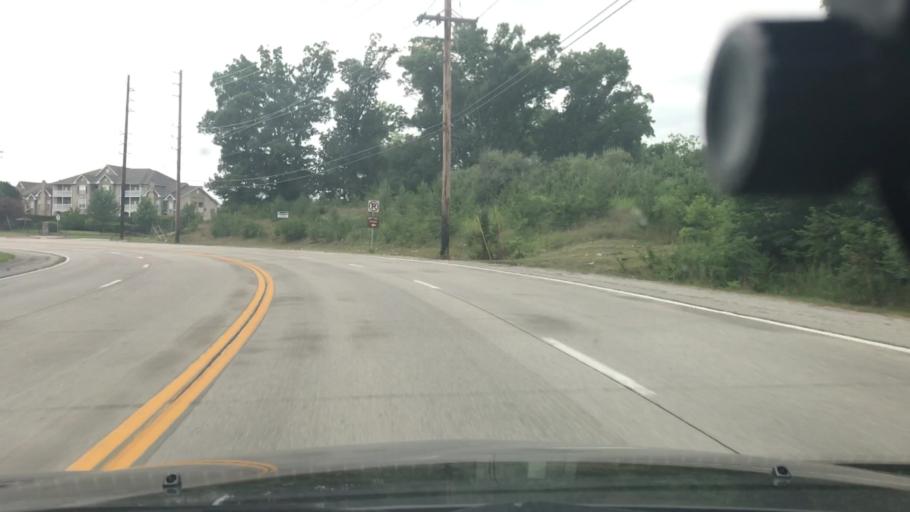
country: US
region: Missouri
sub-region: Saint Charles County
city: Saint Charles
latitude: 38.7449
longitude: -90.5264
